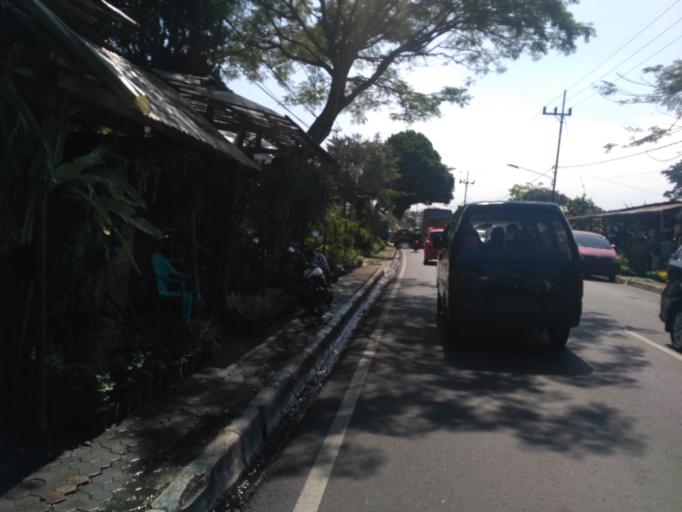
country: ID
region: East Java
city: Batu
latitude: -7.8551
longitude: 112.5271
